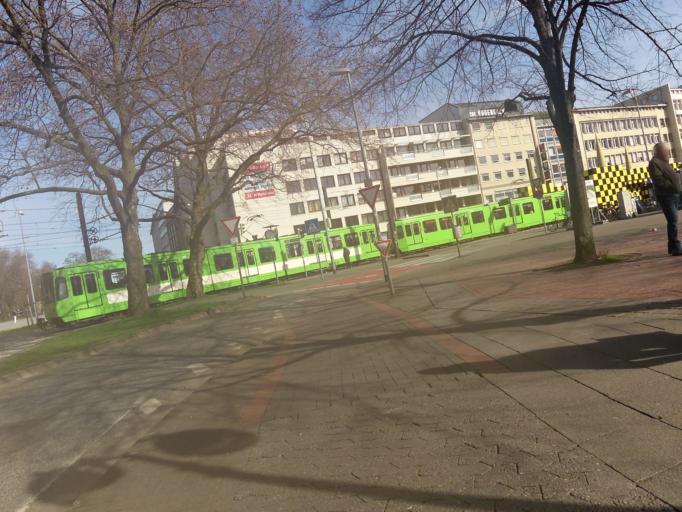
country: DE
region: Lower Saxony
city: Hannover
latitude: 52.3764
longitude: 9.7324
